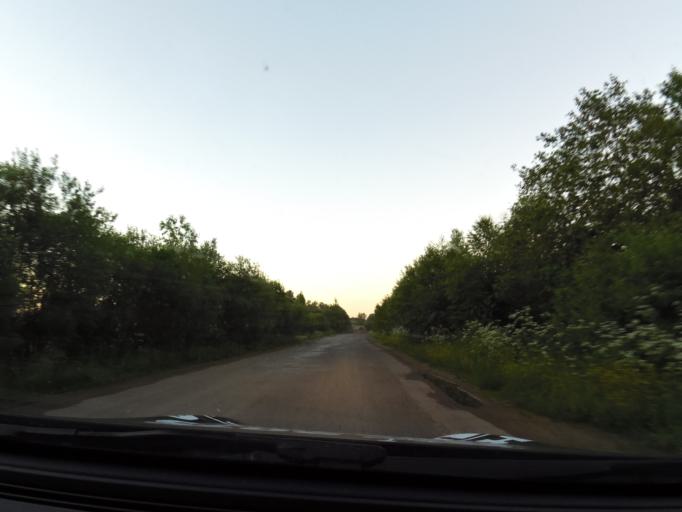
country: RU
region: Leningrad
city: Voznesen'ye
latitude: 60.8364
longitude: 35.7655
